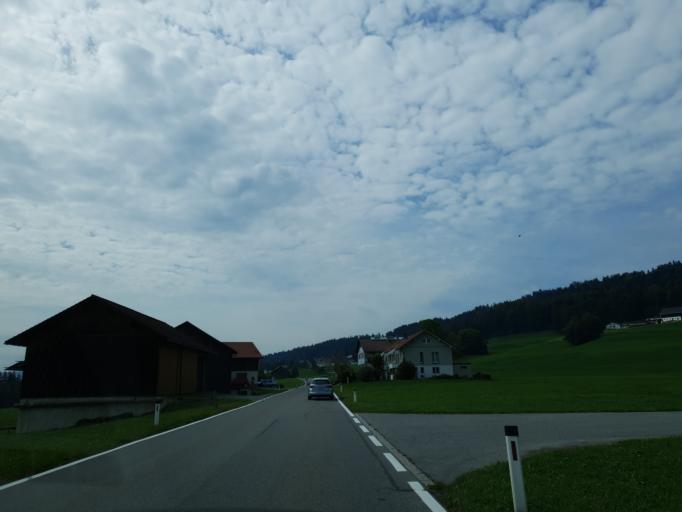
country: AT
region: Vorarlberg
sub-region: Politischer Bezirk Bregenz
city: Sulzberg
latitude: 47.4967
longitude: 9.9084
